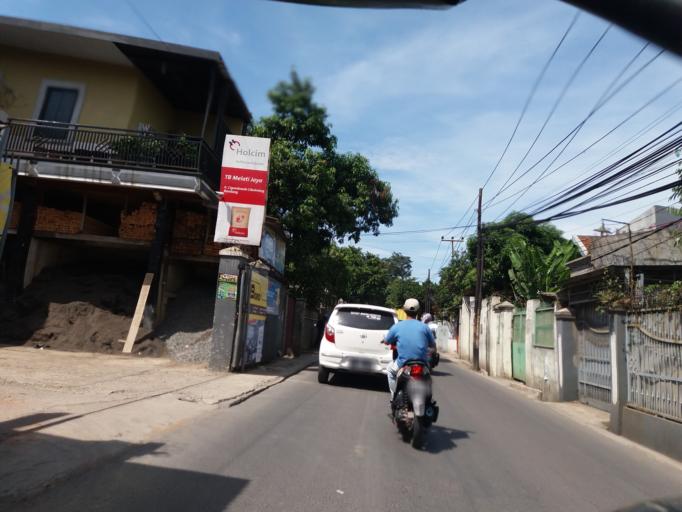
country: ID
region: West Java
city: Margahayukencana
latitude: -6.9502
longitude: 107.5722
